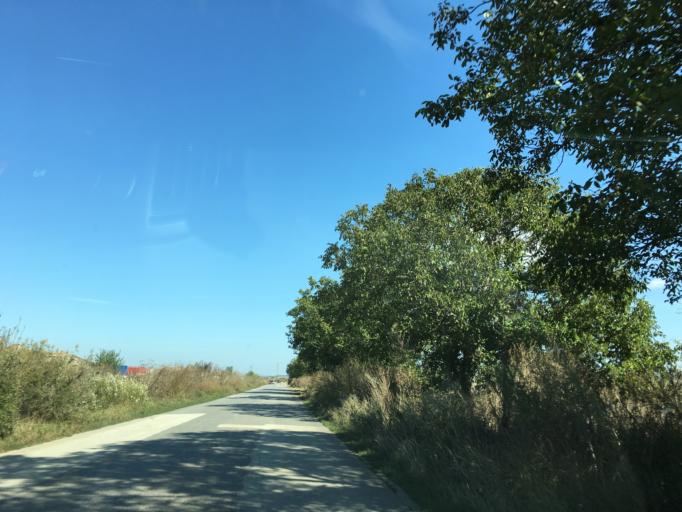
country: RO
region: Olt
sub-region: Comuna Orlea
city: Orlea
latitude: 43.6230
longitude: 24.3807
